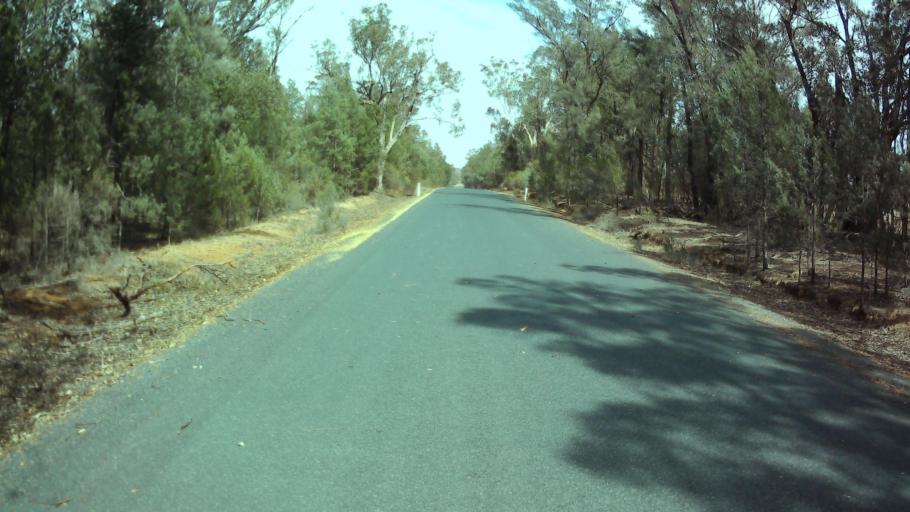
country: AU
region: New South Wales
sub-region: Weddin
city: Grenfell
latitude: -33.8025
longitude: 148.0185
